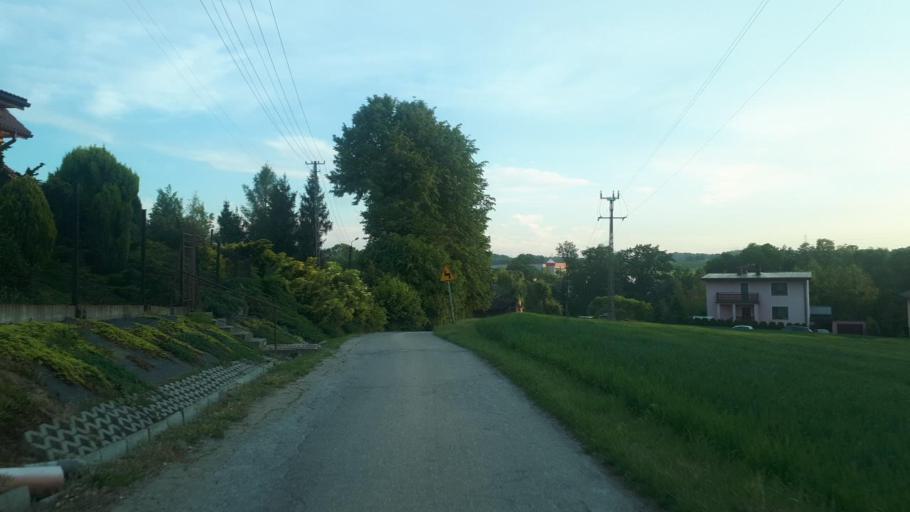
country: PL
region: Silesian Voivodeship
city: Janowice
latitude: 49.9147
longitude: 19.1145
